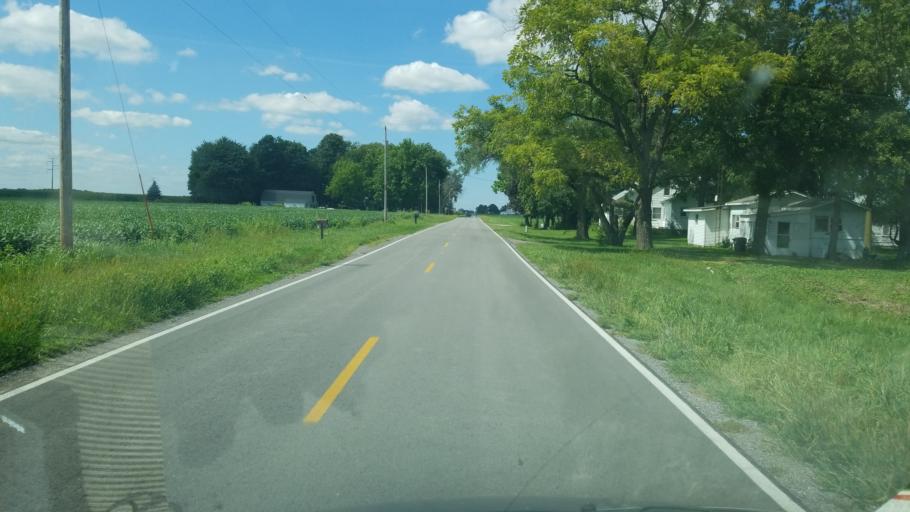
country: US
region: Ohio
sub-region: Fulton County
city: Swanton
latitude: 41.6032
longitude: -83.9510
